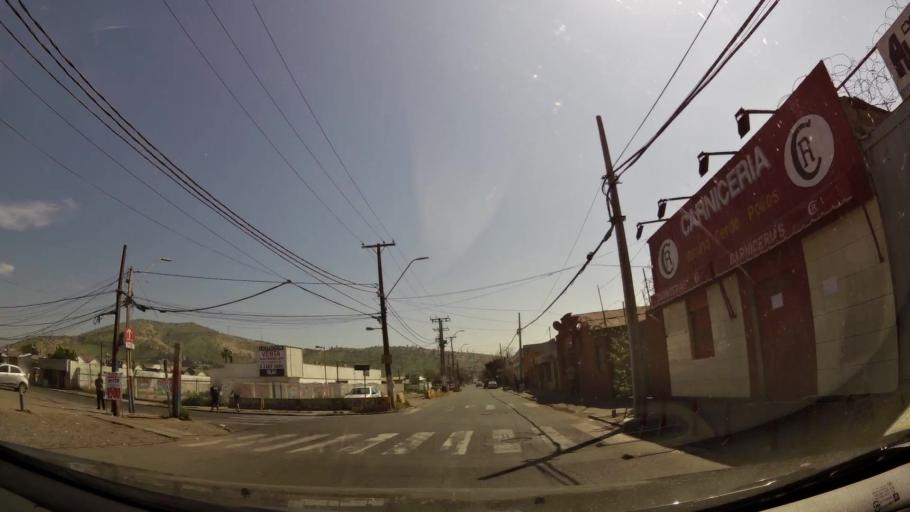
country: CL
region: Santiago Metropolitan
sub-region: Provincia de Santiago
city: Lo Prado
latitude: -33.4008
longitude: -70.7214
